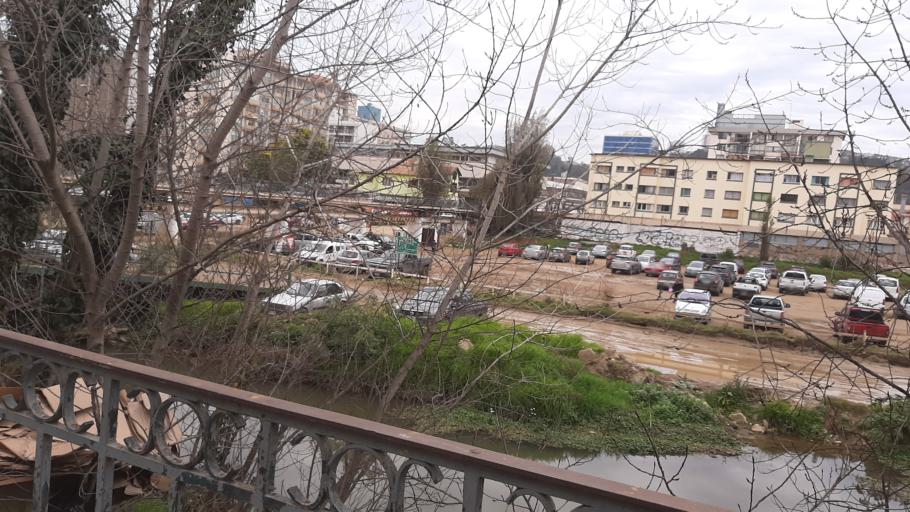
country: CL
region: Valparaiso
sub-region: Provincia de Valparaiso
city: Vina del Mar
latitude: -33.0222
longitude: -71.5540
